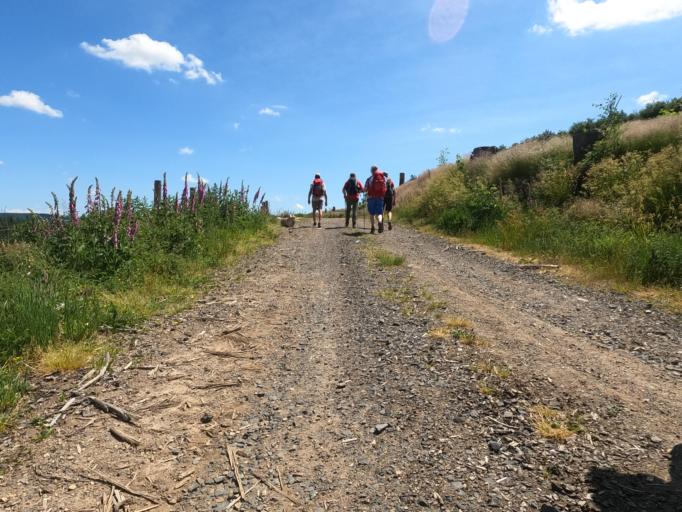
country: DE
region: Rheinland-Pfalz
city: Alpenrod
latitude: 50.6479
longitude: 7.8675
